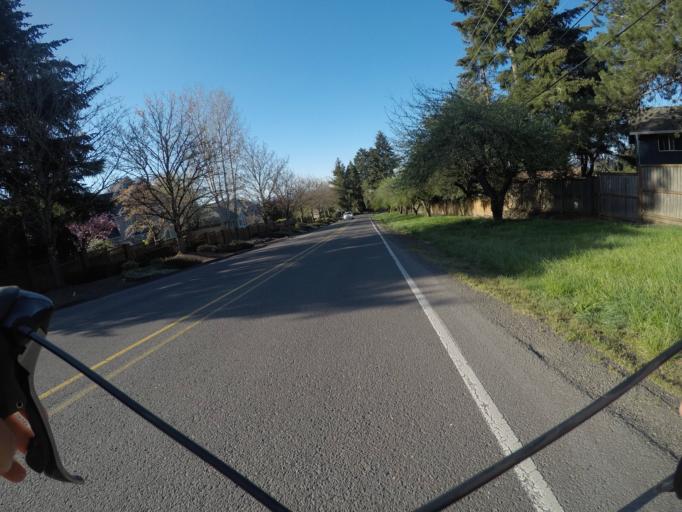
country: US
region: Oregon
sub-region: Washington County
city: Aloha
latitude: 45.4623
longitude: -122.8674
